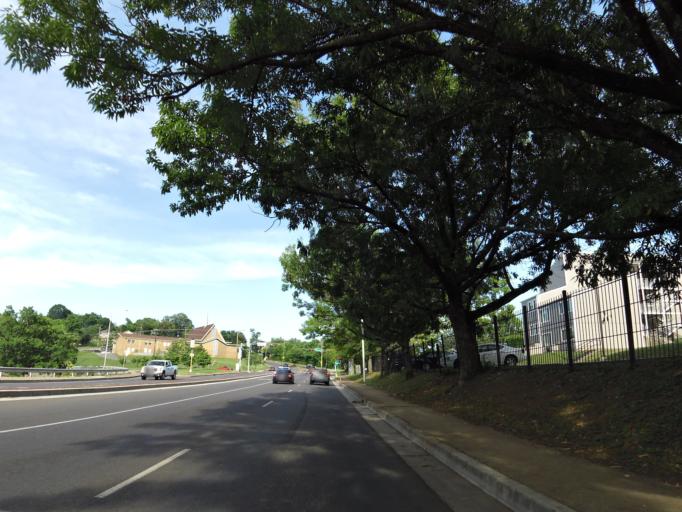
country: US
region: Tennessee
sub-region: Knox County
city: Knoxville
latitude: 35.9703
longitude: -83.9081
